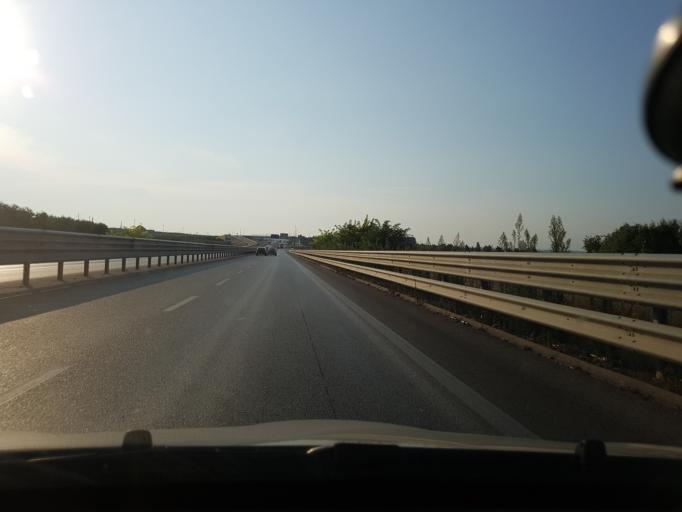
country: IT
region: Apulia
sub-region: Provincia di Foggia
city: Cerignola
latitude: 41.2833
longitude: 15.8484
